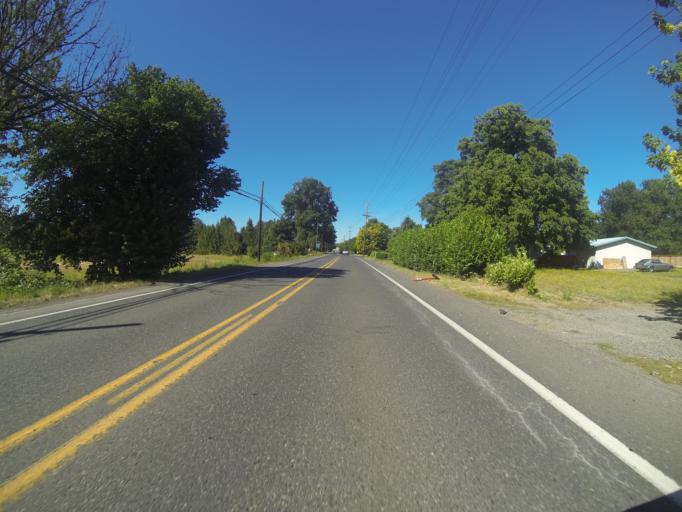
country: US
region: Washington
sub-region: Cowlitz County
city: Woodland
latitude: 45.9189
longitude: -122.7332
